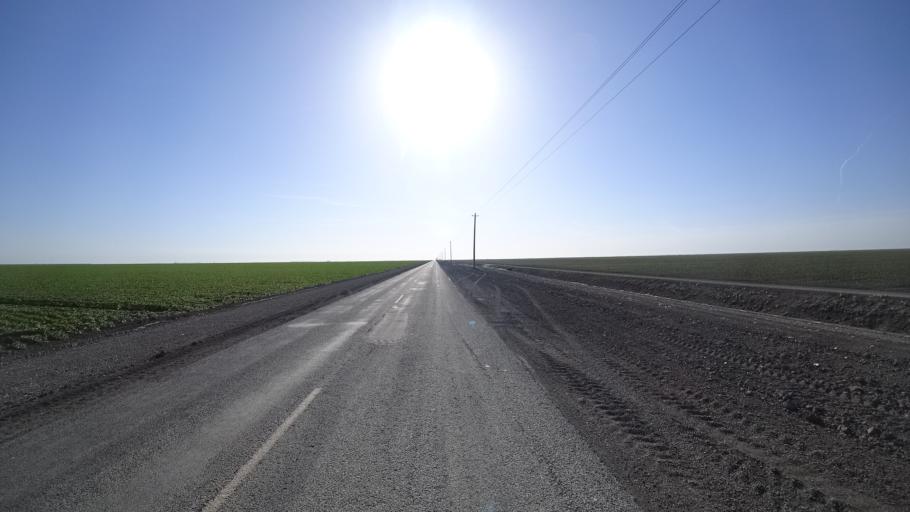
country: US
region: California
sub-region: Kings County
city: Stratford
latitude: 36.0797
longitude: -119.7476
